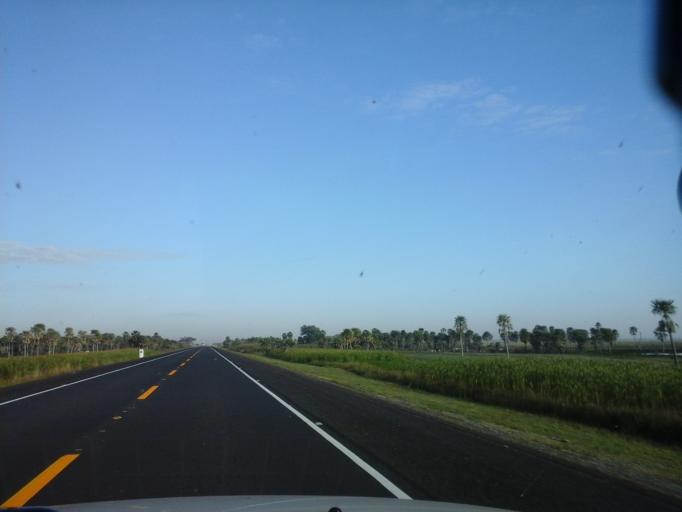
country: PY
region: Neembucu
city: Pilar
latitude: -26.8658
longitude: -57.8251
